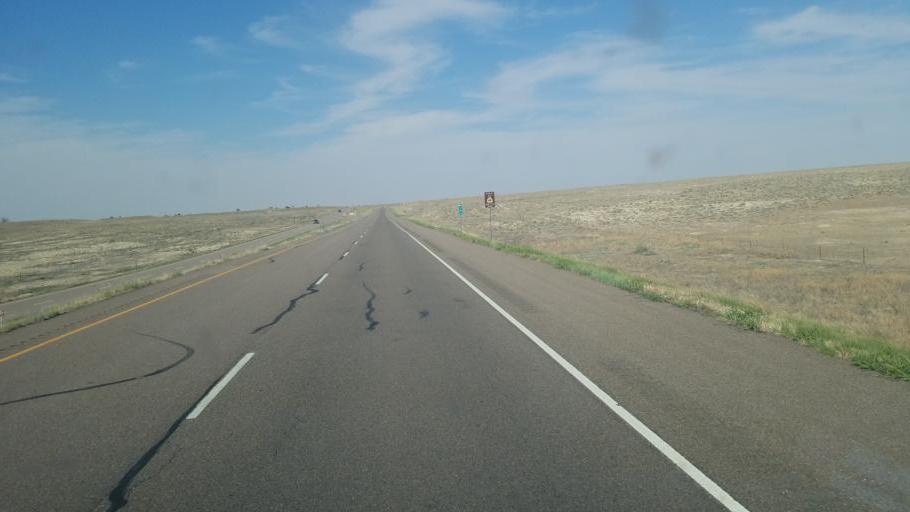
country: US
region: Colorado
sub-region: Otero County
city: La Junta
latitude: 38.0016
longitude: -103.4696
